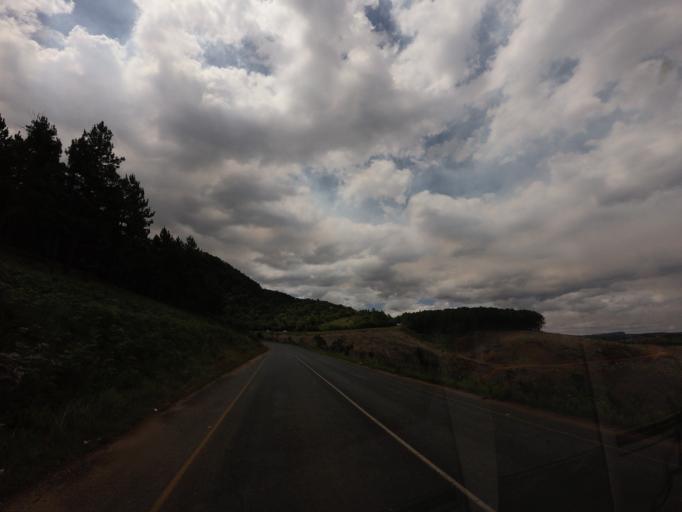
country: ZA
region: Mpumalanga
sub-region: Ehlanzeni District
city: Graksop
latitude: -24.9471
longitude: 30.8115
